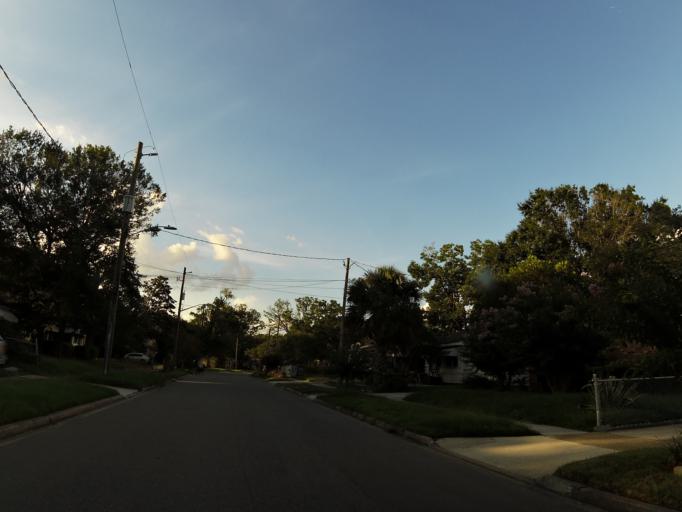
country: US
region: Florida
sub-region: Duval County
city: Jacksonville
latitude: 30.3451
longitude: -81.6925
